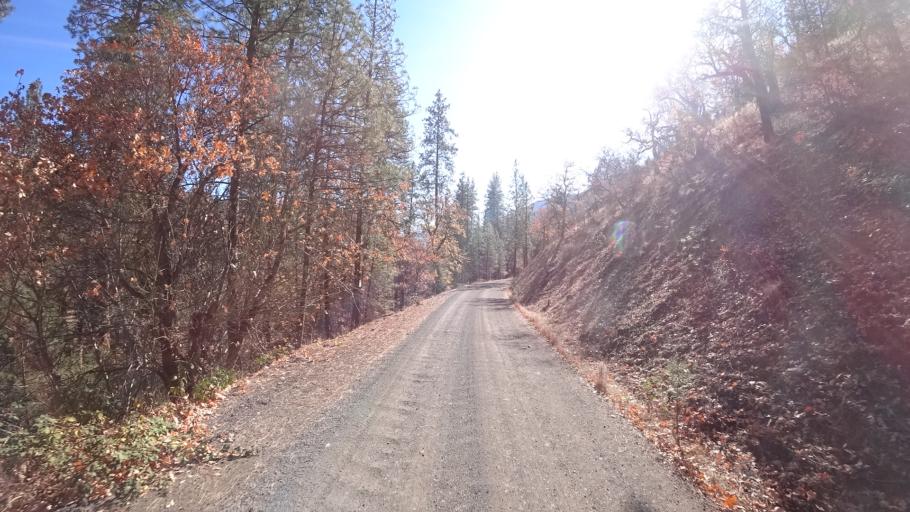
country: US
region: California
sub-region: Siskiyou County
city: Yreka
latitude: 41.8626
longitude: -122.7079
